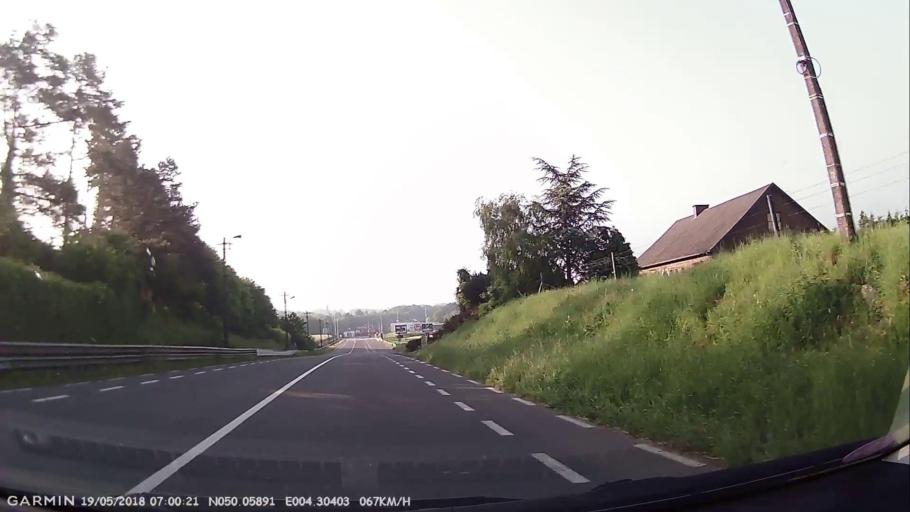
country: BE
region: Wallonia
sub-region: Province du Hainaut
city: Chimay
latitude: 50.0588
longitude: 4.3042
